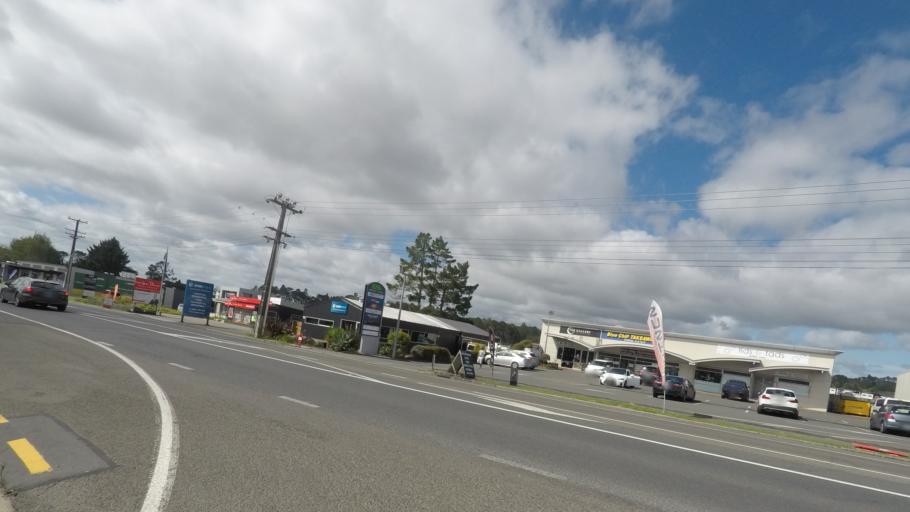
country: NZ
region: Auckland
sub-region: Auckland
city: Muriwai Beach
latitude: -36.7720
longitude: 174.5445
